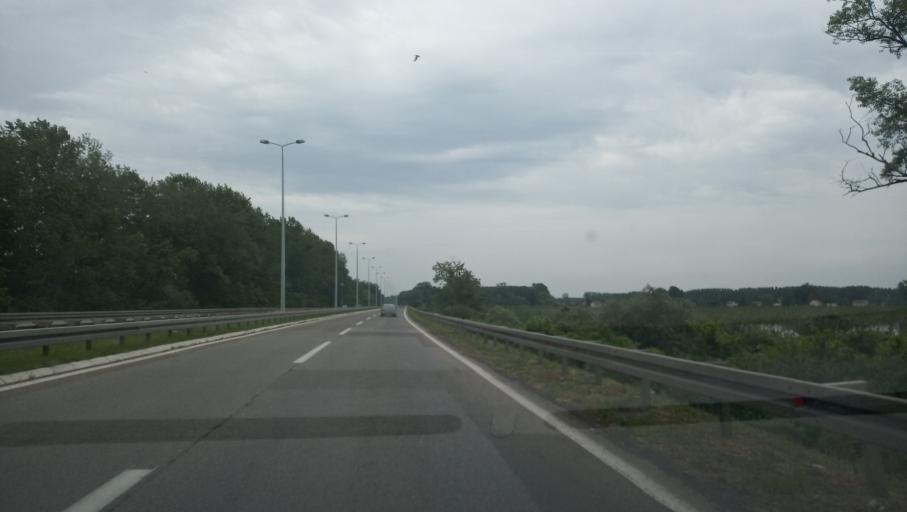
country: RS
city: Ovca
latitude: 44.8623
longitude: 20.5851
